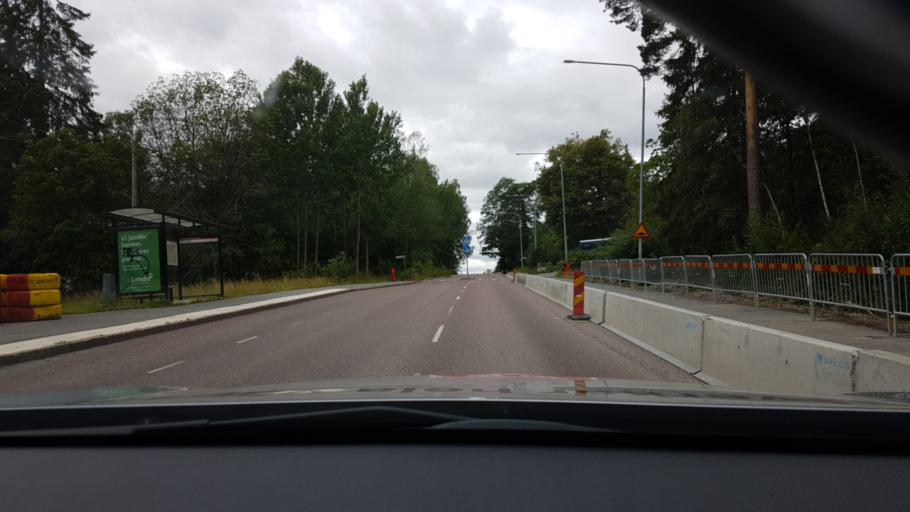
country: SE
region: Stockholm
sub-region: Huddinge Kommun
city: Huddinge
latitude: 59.2452
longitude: 18.0196
